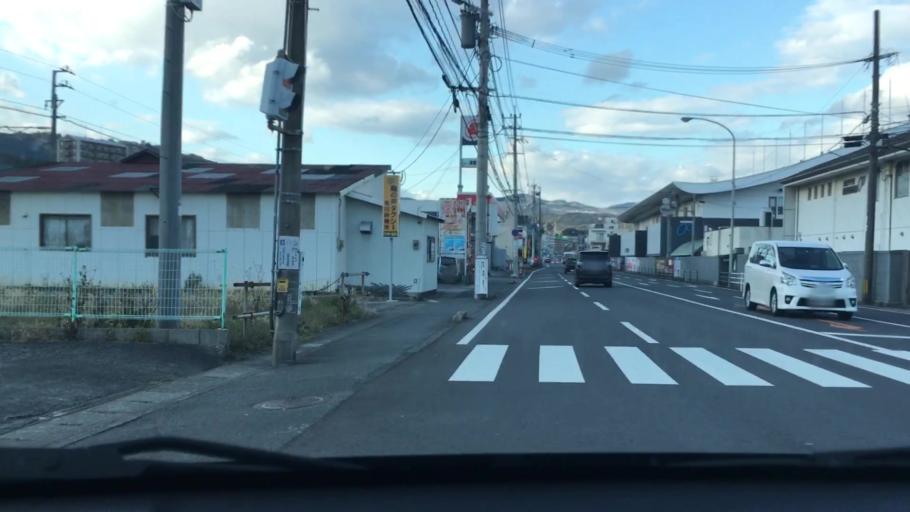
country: JP
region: Oita
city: Beppu
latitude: 33.3211
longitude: 131.4981
